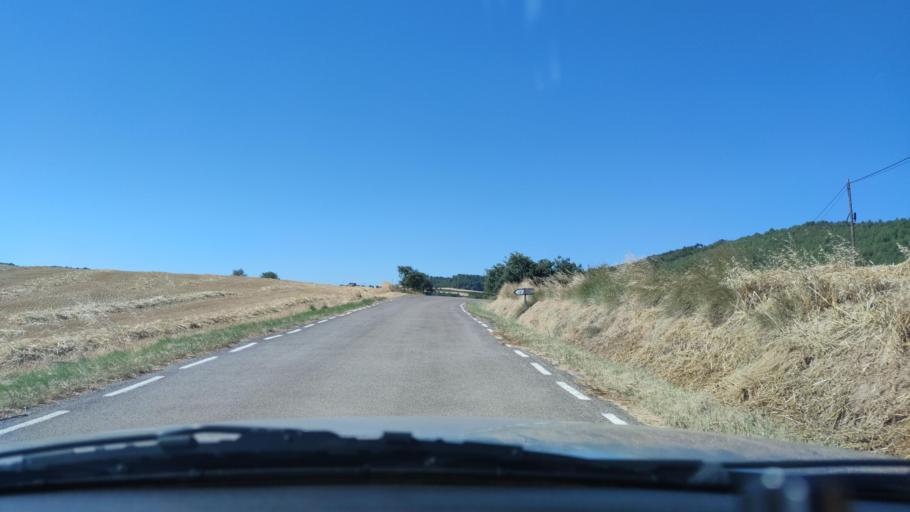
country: ES
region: Catalonia
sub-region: Provincia de Lleida
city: Solsona
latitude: 41.9657
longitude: 1.4963
